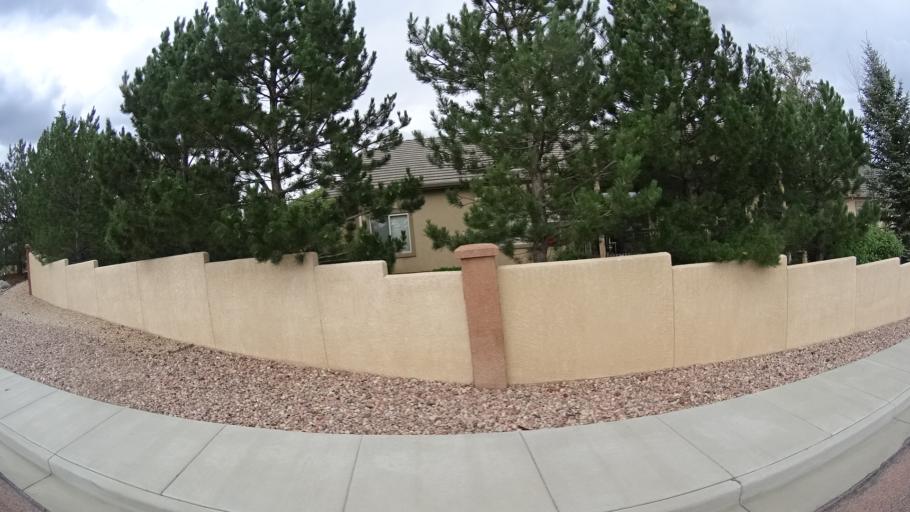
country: US
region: Colorado
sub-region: El Paso County
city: Woodmoor
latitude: 39.0954
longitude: -104.8586
